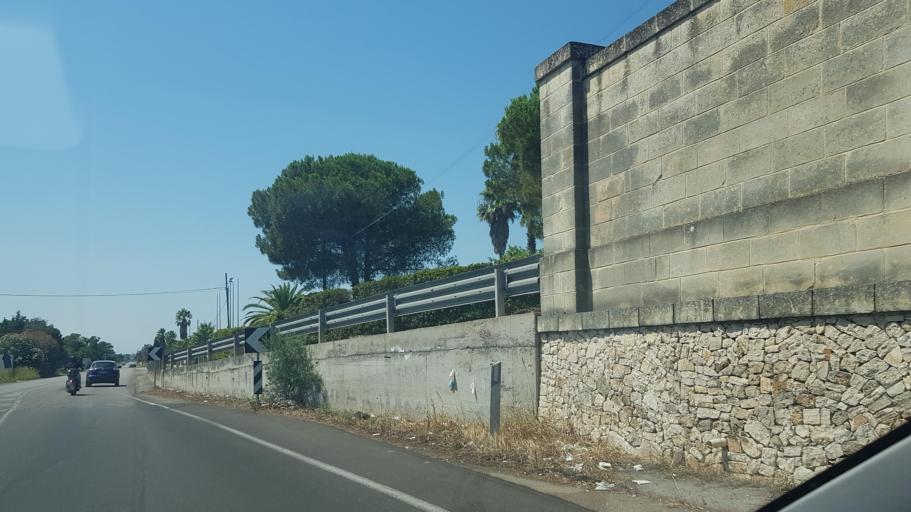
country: IT
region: Apulia
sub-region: Provincia di Lecce
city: Merine
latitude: 40.3400
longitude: 18.2216
